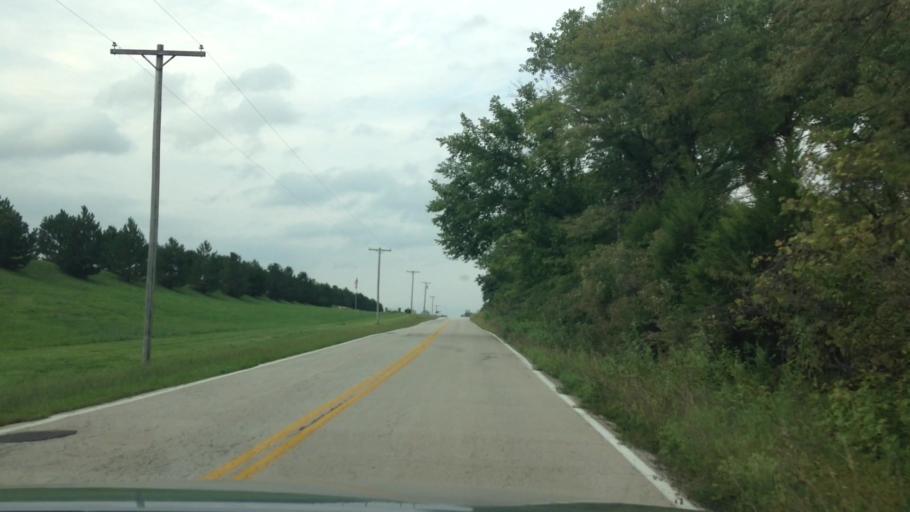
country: US
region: Missouri
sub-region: Platte County
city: Platte City
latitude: 39.3446
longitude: -94.6802
